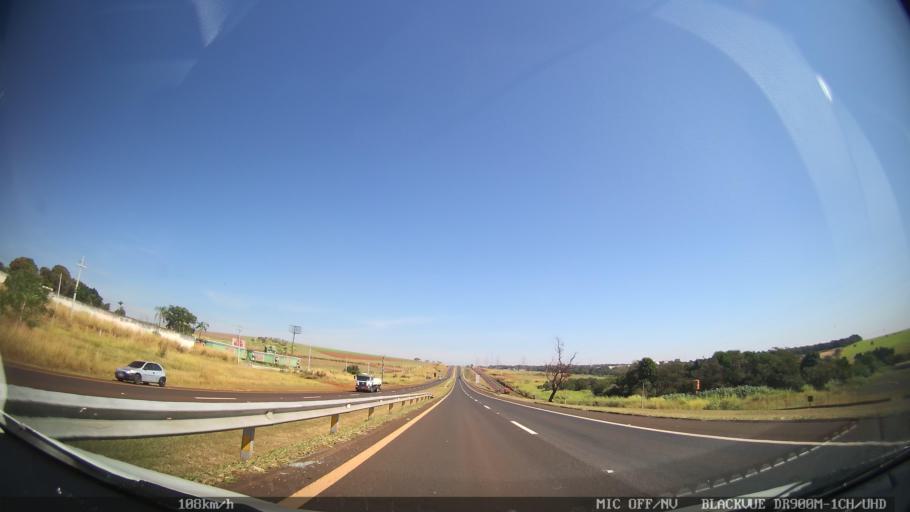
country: BR
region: Sao Paulo
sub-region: Ribeirao Preto
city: Ribeirao Preto
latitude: -21.1391
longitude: -47.8655
